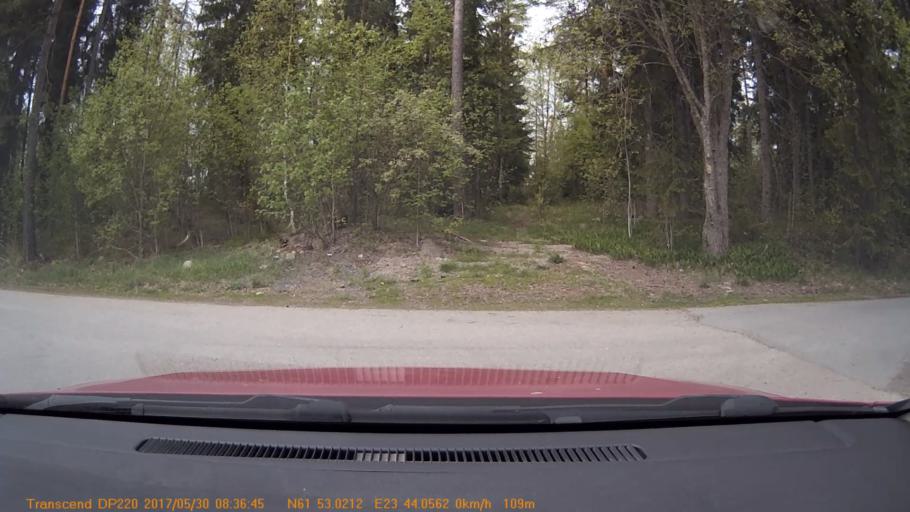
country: FI
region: Pirkanmaa
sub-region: Tampere
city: Kuru
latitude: 61.8837
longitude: 23.7343
